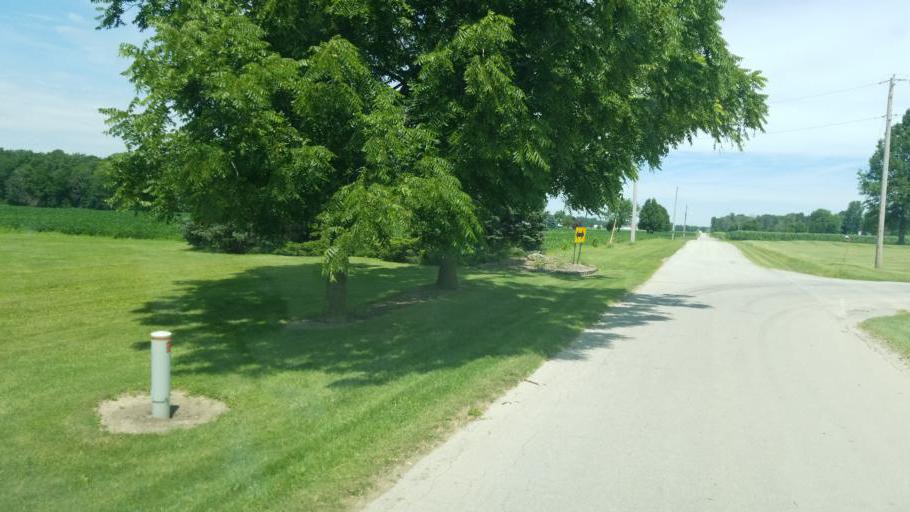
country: US
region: Ohio
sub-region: Crawford County
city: Bucyrus
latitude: 40.8778
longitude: -82.9210
